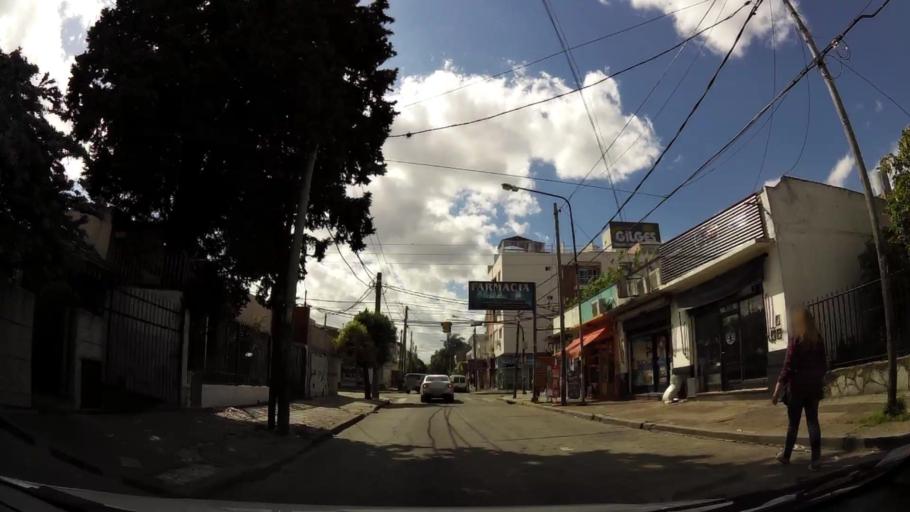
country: AR
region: Buenos Aires
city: San Justo
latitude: -34.6491
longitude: -58.5559
